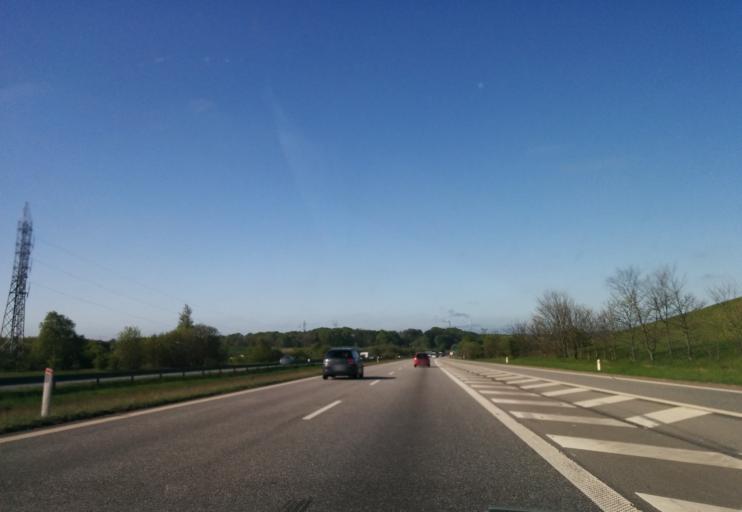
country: DK
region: Central Jutland
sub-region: Skanderborg Kommune
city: Stilling
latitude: 56.0645
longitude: 9.9727
